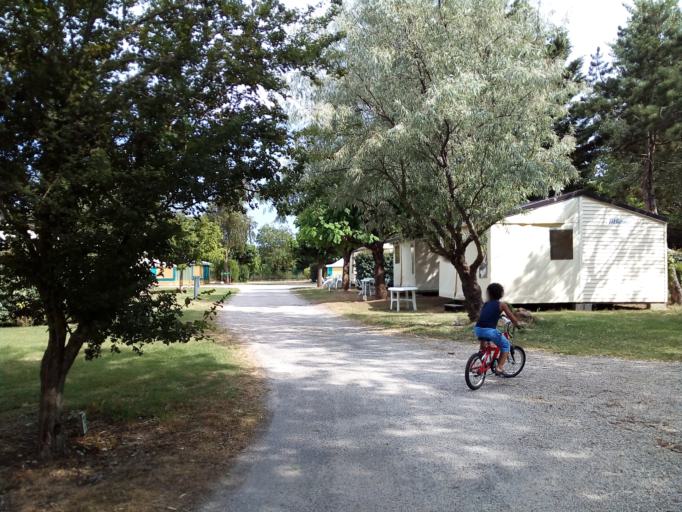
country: FR
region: Poitou-Charentes
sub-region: Departement de la Charente-Maritime
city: Boyard-Ville
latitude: 45.9492
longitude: -1.2470
